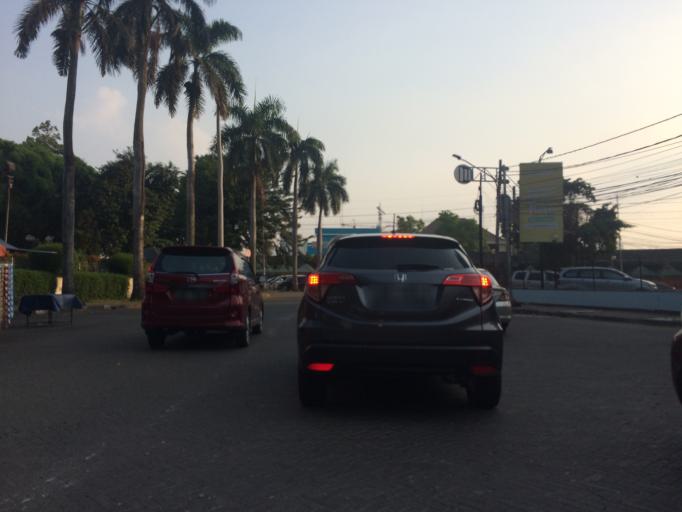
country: ID
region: Jakarta Raya
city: Jakarta
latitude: -6.2030
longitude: 106.8456
